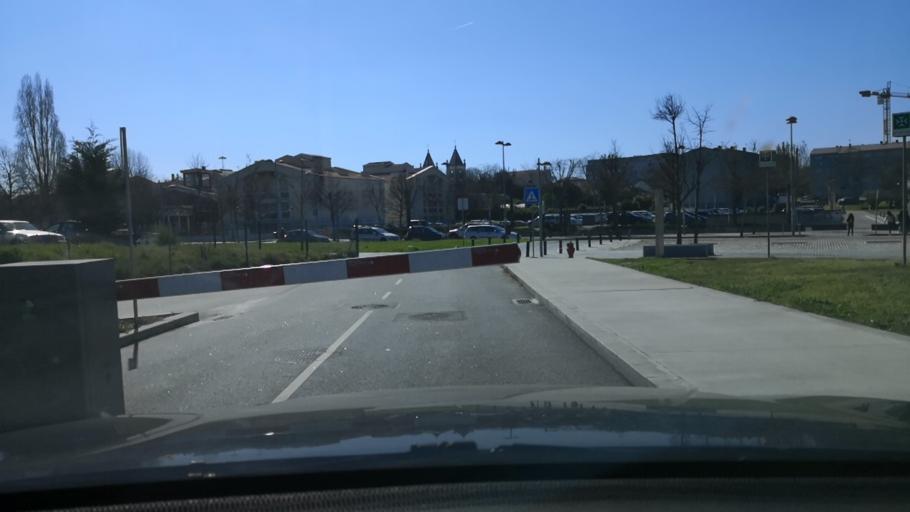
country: PT
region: Porto
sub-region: Matosinhos
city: Sao Mamede de Infesta
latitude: 41.1750
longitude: -8.6031
